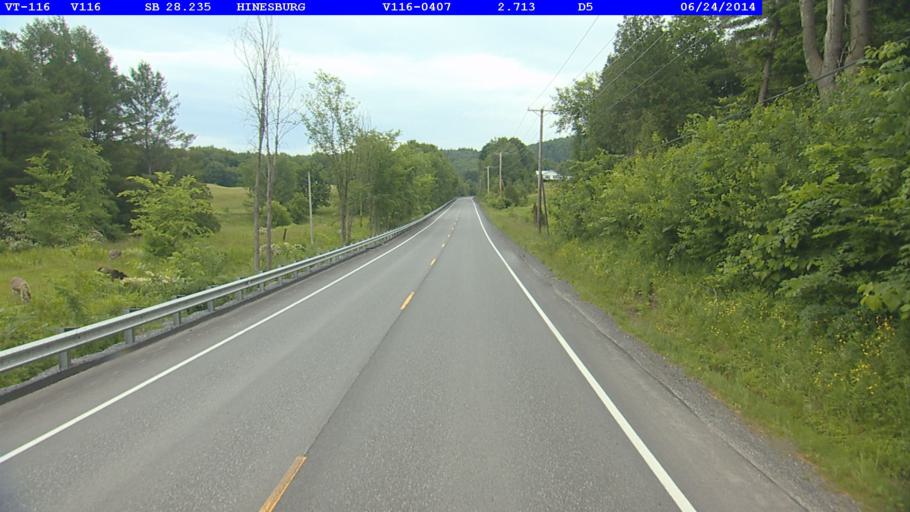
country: US
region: Vermont
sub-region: Chittenden County
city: Hinesburg
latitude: 44.3143
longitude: -73.0837
